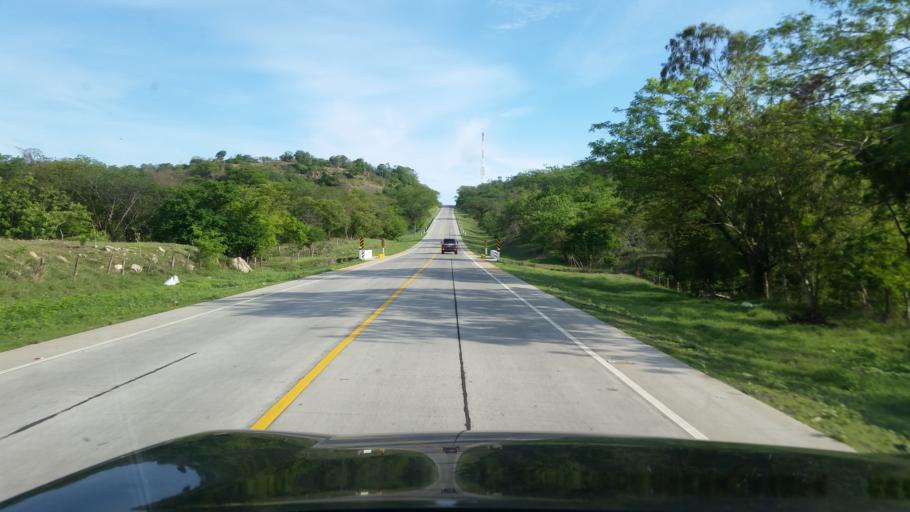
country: NI
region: Leon
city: Nagarote
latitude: 12.1654
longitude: -86.6611
